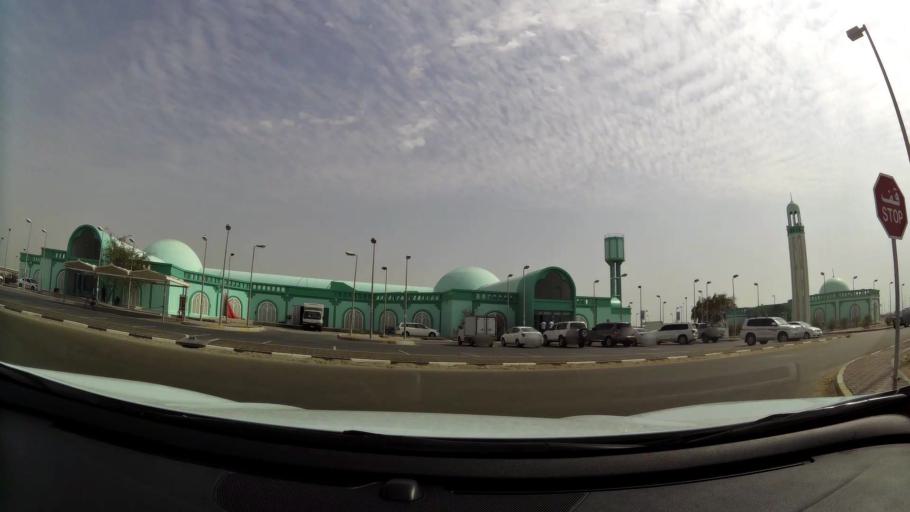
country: AE
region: Abu Dhabi
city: Abu Dhabi
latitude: 24.5446
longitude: 54.6855
